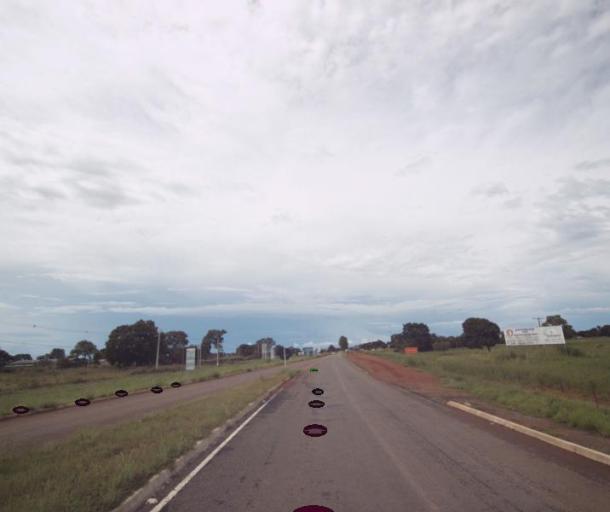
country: BR
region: Goias
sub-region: Sao Miguel Do Araguaia
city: Sao Miguel do Araguaia
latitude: -13.2839
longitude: -50.1821
